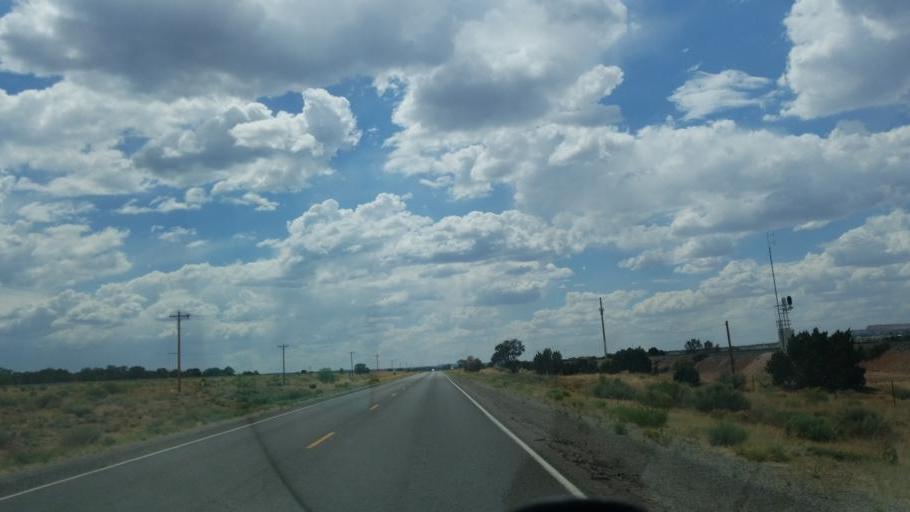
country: US
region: New Mexico
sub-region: McKinley County
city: Thoreau
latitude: 35.3895
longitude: -108.1750
